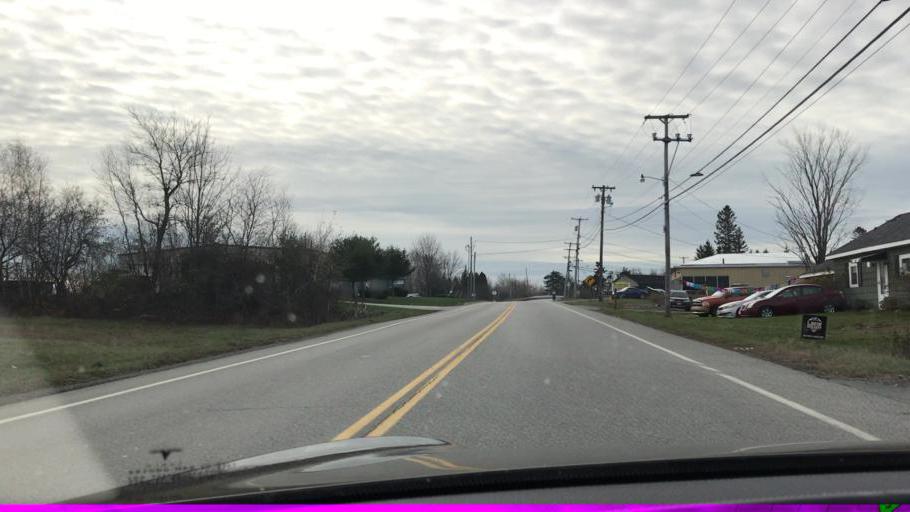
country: US
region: Maine
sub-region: Penobscot County
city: Bangor
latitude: 44.7831
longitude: -68.8158
